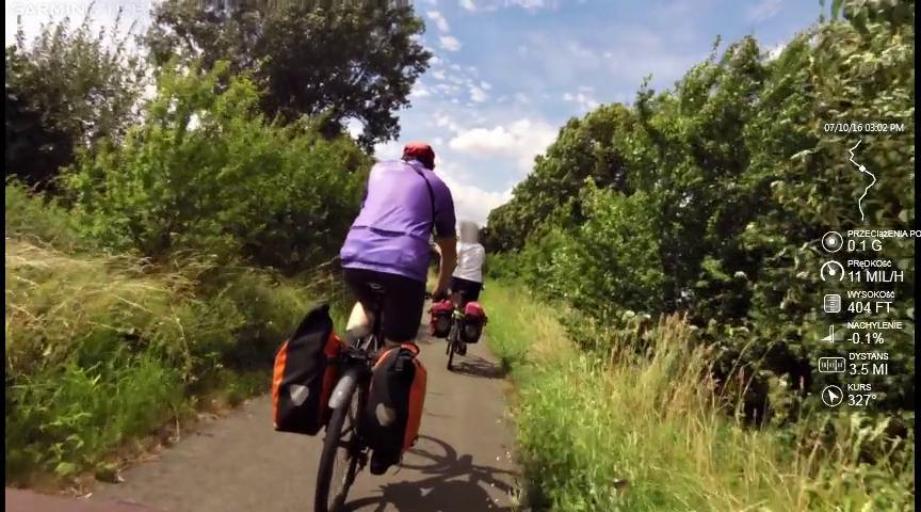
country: PL
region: West Pomeranian Voivodeship
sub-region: Powiat gryfinski
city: Banie
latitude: 53.1131
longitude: 14.6310
